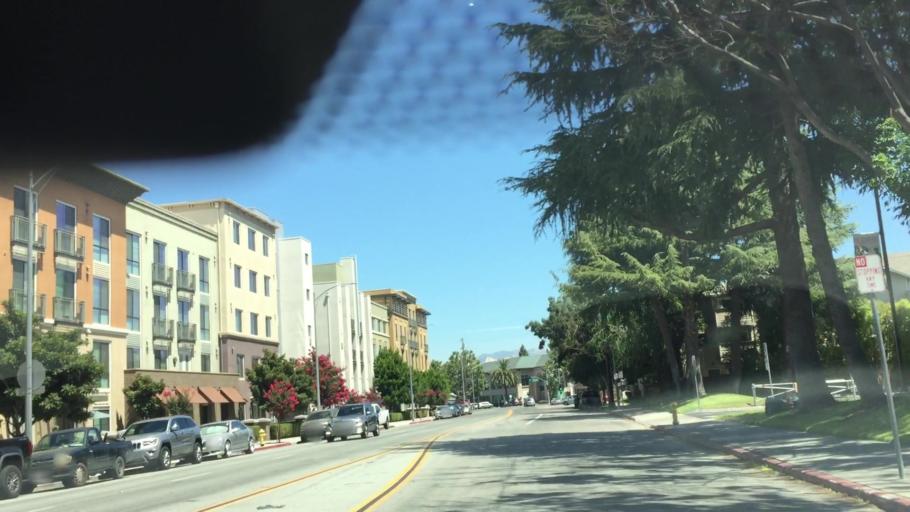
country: US
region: California
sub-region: Santa Clara County
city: Buena Vista
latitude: 37.3166
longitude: -121.9100
